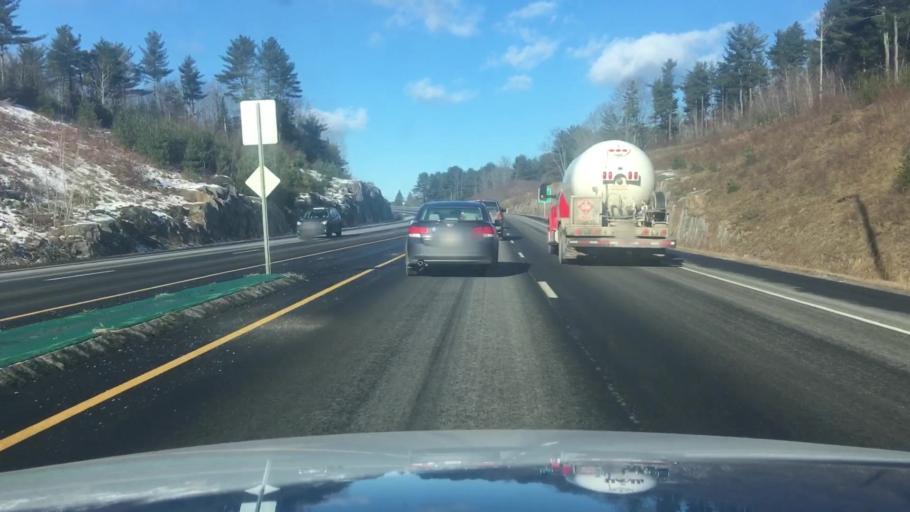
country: US
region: Maine
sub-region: Kennebec County
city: Augusta
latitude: 44.3475
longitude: -69.7723
